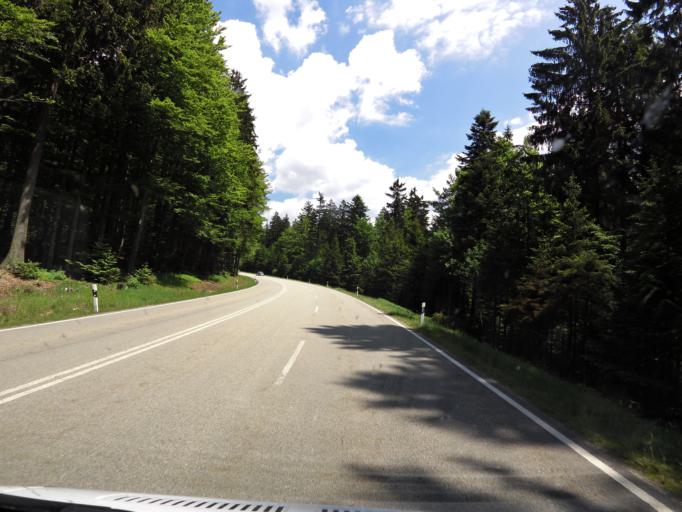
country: DE
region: Bavaria
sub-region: Lower Bavaria
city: Philippsreut
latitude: 48.8465
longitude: 13.6702
